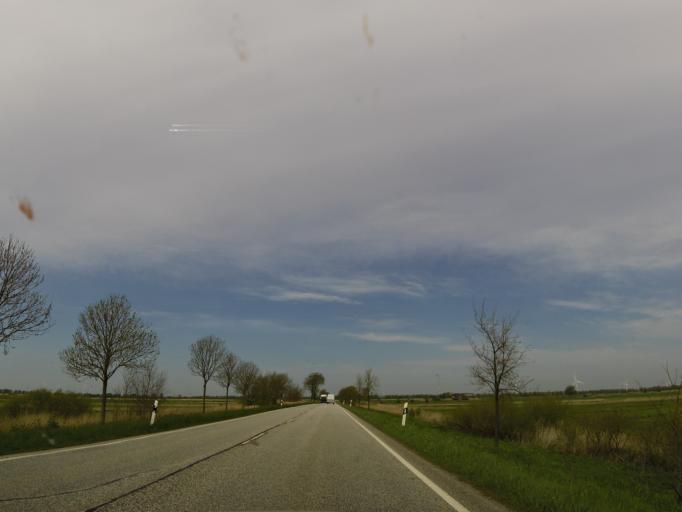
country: DE
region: Schleswig-Holstein
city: Koldenbuttel
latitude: 54.4324
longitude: 9.0508
